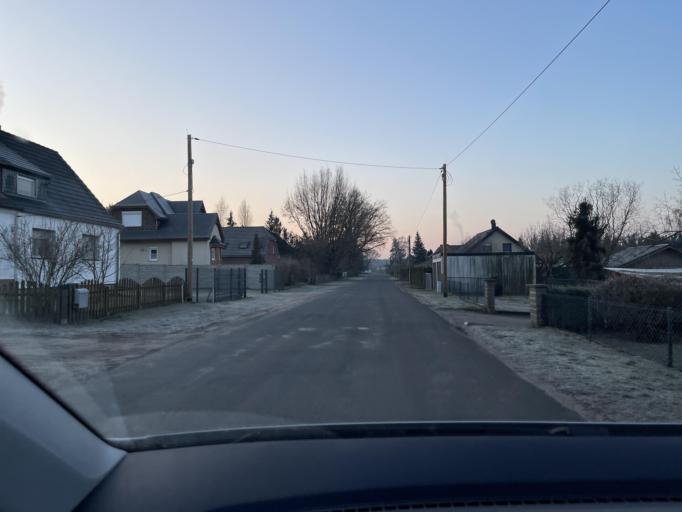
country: DE
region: Brandenburg
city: Roskow
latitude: 52.3910
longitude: 12.6925
